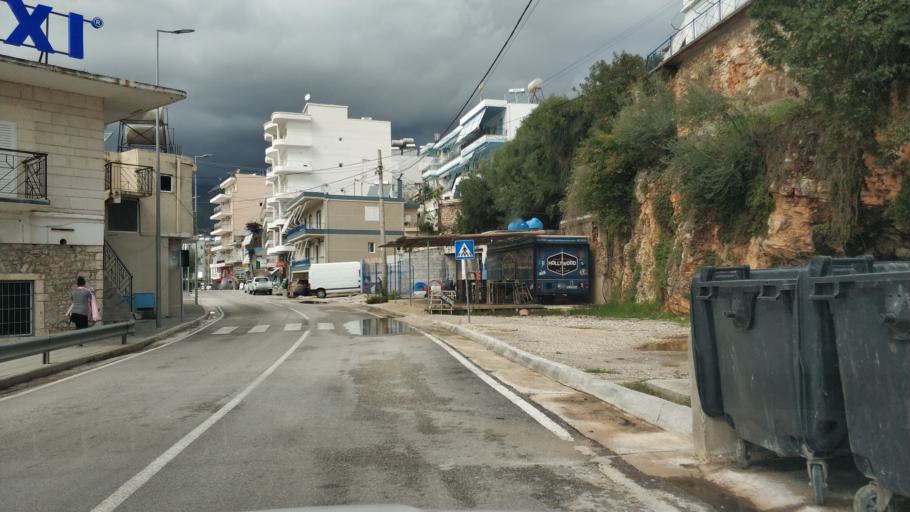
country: AL
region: Vlore
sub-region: Rrethi i Vlores
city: Himare
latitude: 40.1006
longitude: 19.7471
